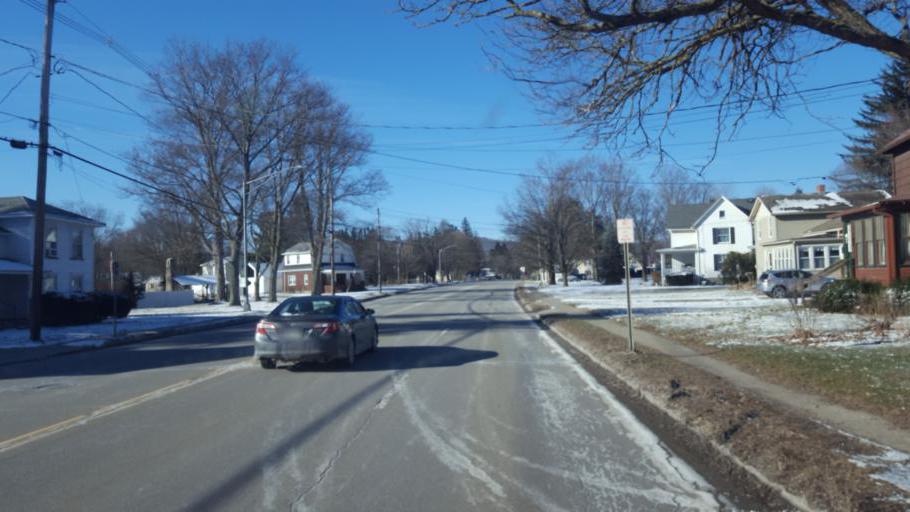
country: US
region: New York
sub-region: Allegany County
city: Wellsville
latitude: 42.1196
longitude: -77.9326
